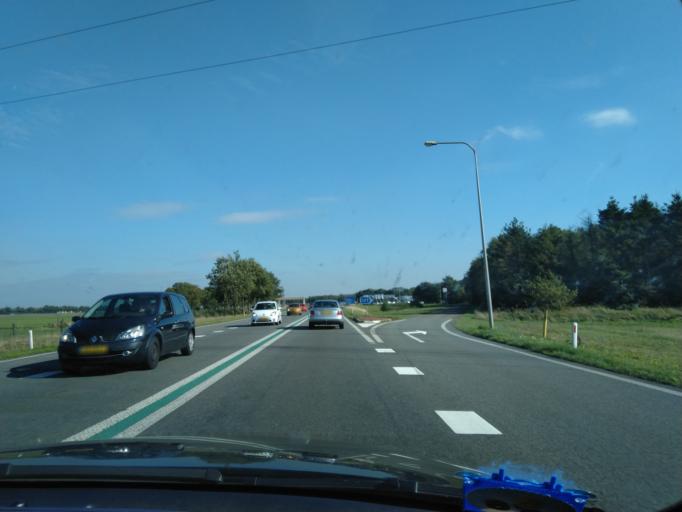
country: NL
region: Groningen
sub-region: Gemeente Pekela
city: Oude Pekela
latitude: 53.0890
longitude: 6.9502
